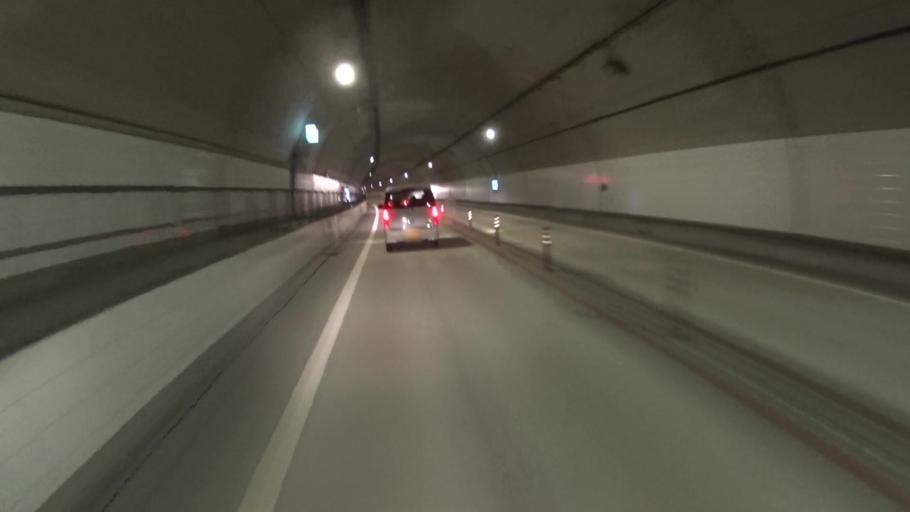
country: JP
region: Kyoto
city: Miyazu
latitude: 35.5283
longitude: 135.1734
